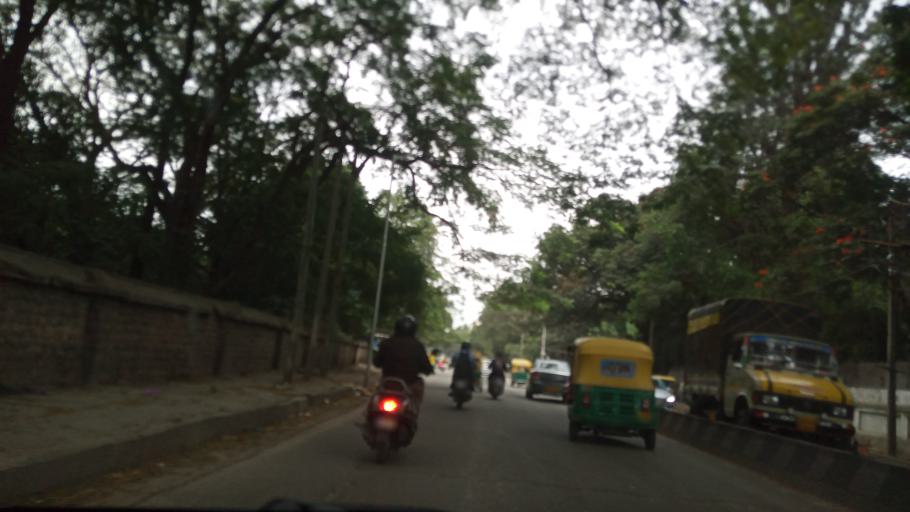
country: IN
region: Karnataka
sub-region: Bangalore Urban
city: Bangalore
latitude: 12.9971
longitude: 77.5957
